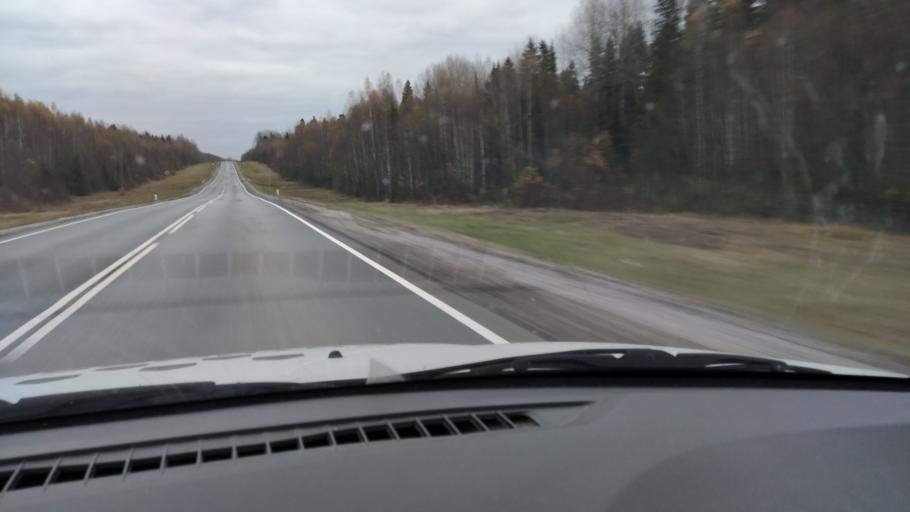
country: RU
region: Kirov
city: Lesnyye Polyany
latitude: 58.8340
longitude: 52.6673
